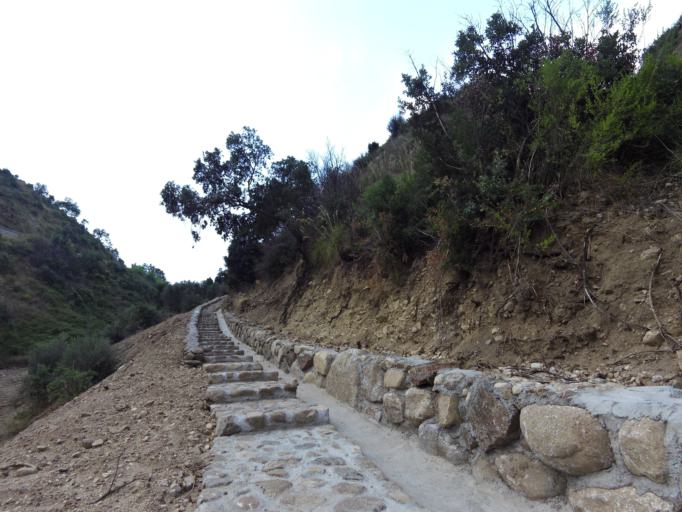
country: IT
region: Calabria
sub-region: Provincia di Reggio Calabria
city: Stilo
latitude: 38.4934
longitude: 16.4713
